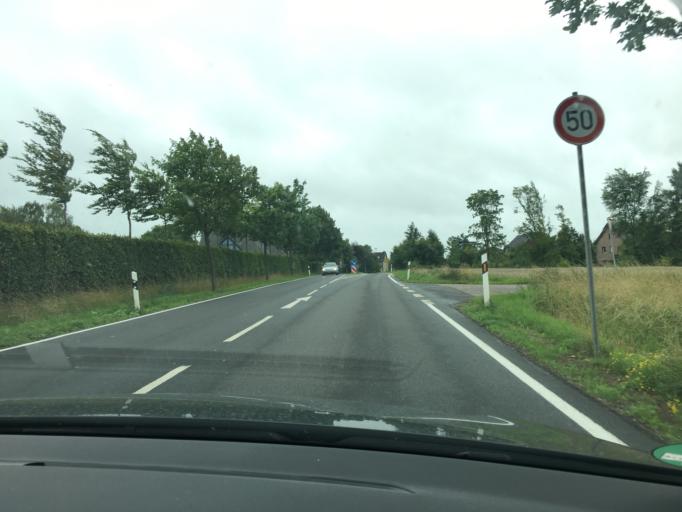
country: DE
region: North Rhine-Westphalia
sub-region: Regierungsbezirk Koln
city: Hurtgenwald
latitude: 50.7289
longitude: 6.3954
